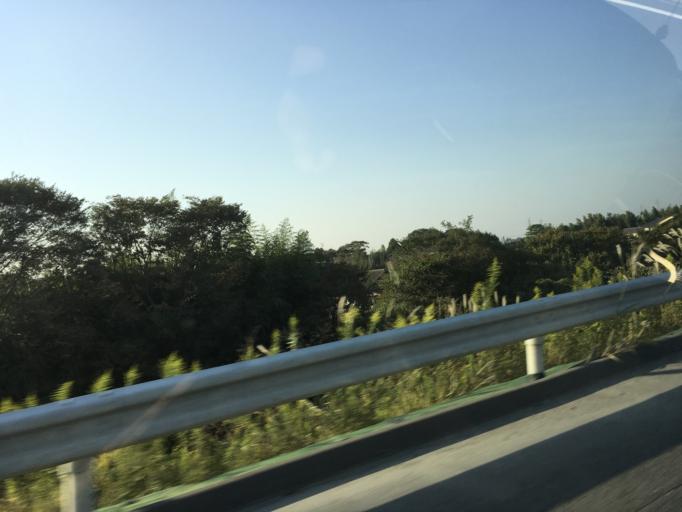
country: JP
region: Miyagi
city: Ishinomaki
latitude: 38.4525
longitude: 141.2718
